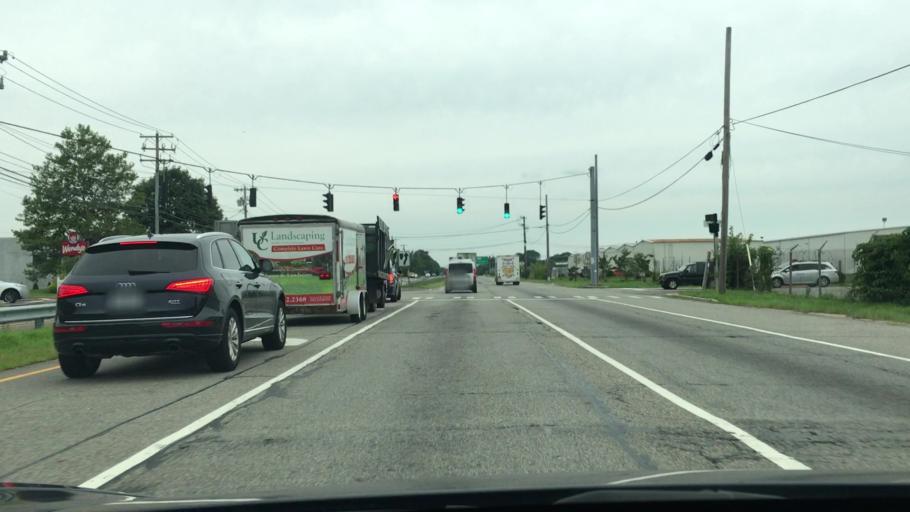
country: US
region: New York
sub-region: Suffolk County
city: East Farmingdale
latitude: 40.7206
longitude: -73.4174
